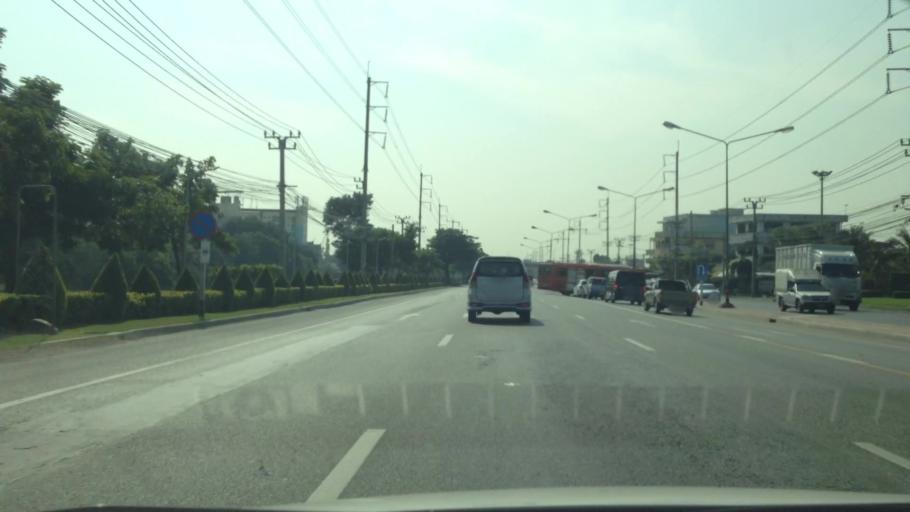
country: TH
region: Samut Prakan
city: Samut Prakan
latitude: 13.5563
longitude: 100.6132
